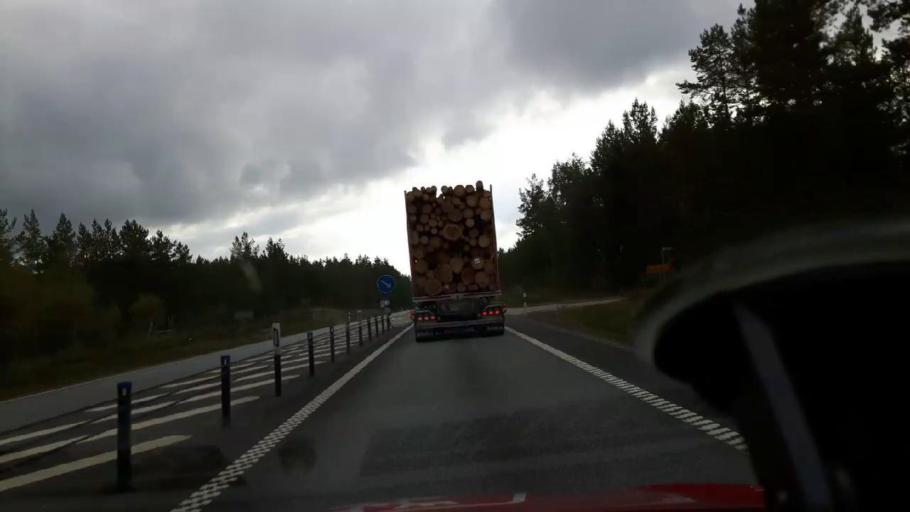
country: SE
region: Gaevleborg
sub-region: Gavle Kommun
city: Norrsundet
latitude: 61.0240
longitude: 16.9760
